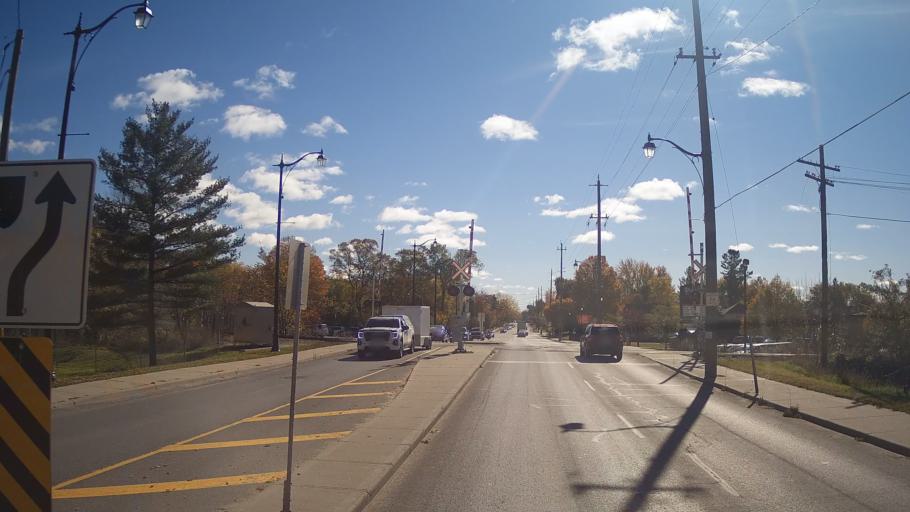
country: CA
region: Ontario
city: Perth
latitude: 44.9075
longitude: -76.2613
